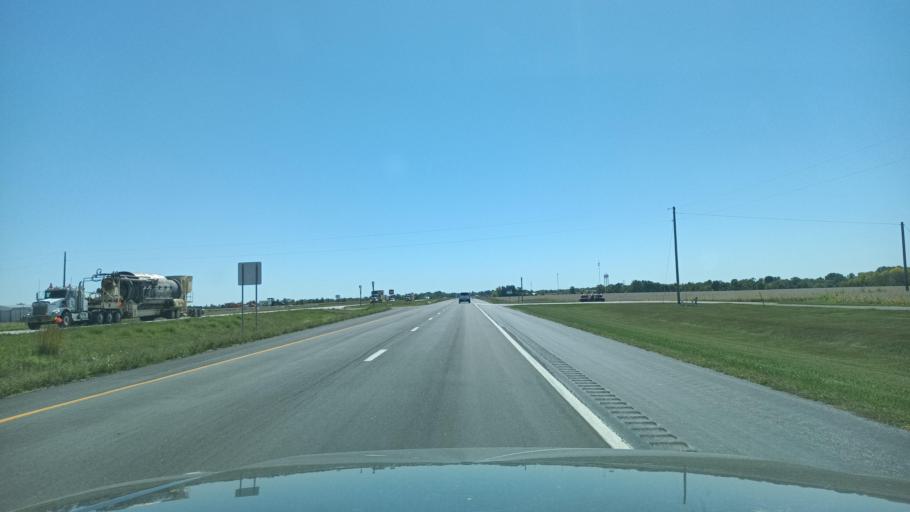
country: US
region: Missouri
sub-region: Macon County
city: La Plata
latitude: 40.0516
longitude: -92.4942
